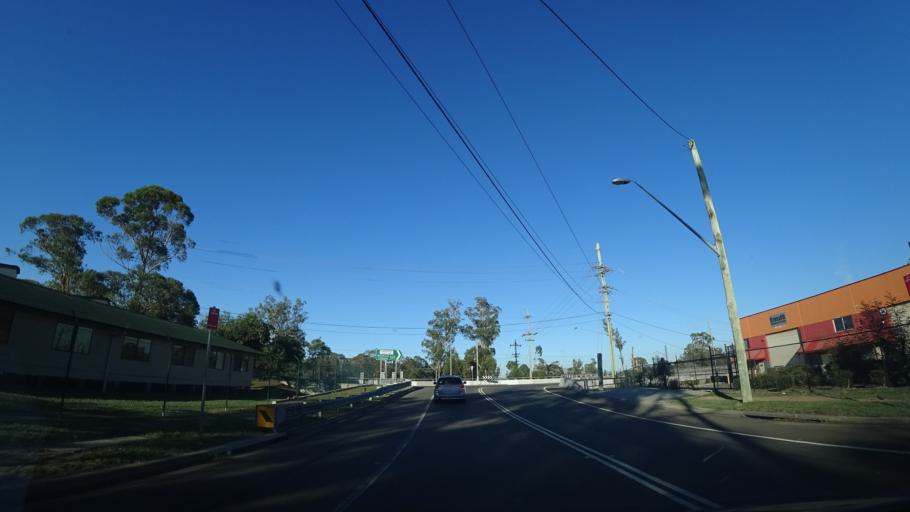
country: AU
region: New South Wales
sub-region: Hawkesbury
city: South Windsor
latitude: -33.6278
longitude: 150.8346
